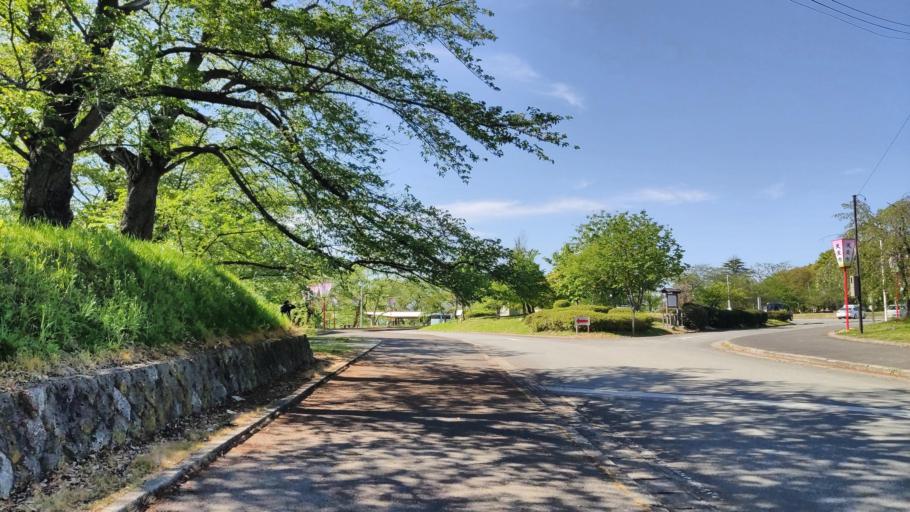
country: JP
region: Yamagata
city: Tendo
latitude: 38.3522
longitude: 140.3756
